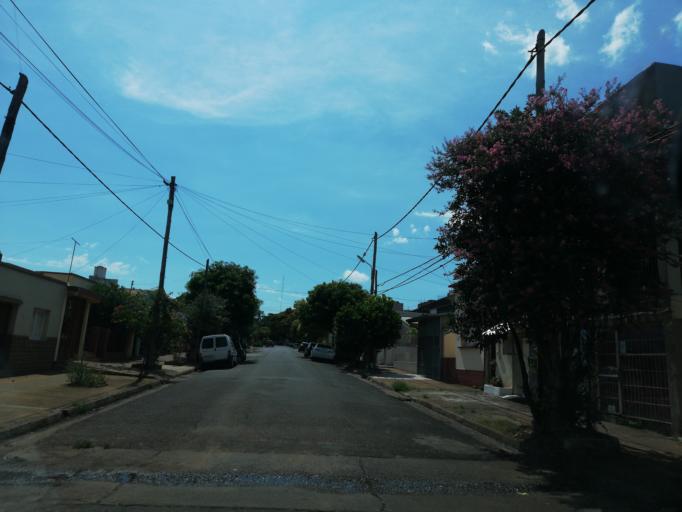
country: AR
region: Misiones
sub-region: Departamento de Capital
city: Posadas
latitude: -27.3775
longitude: -55.8961
